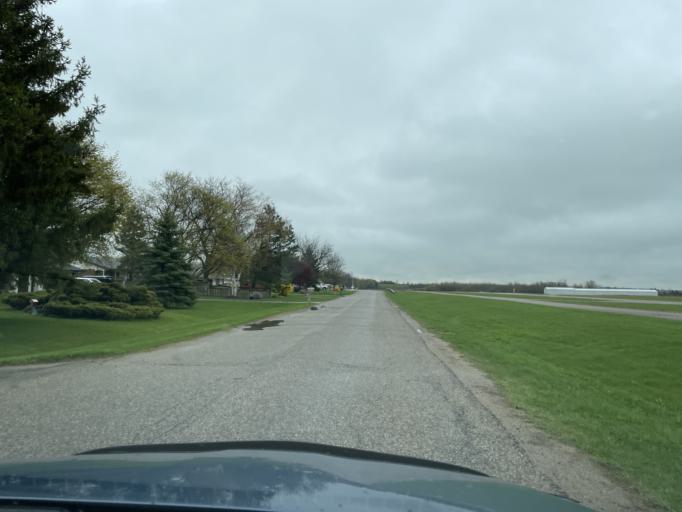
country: CA
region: Ontario
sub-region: Wellington County
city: Guelph
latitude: 43.5651
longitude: -80.1977
